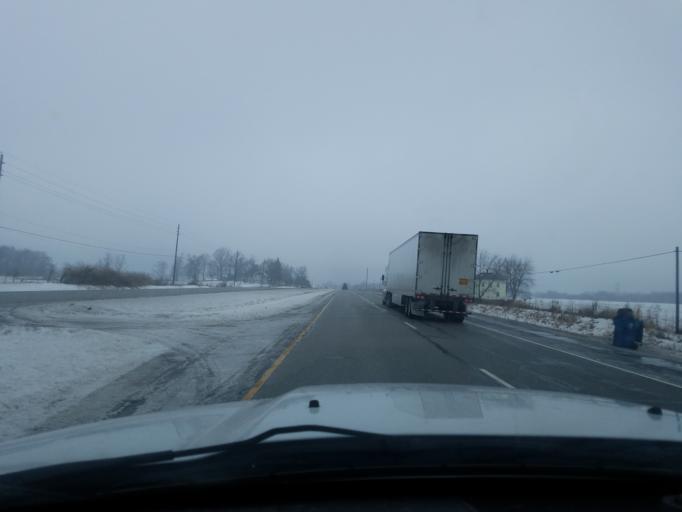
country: US
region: Indiana
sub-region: Miami County
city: Grissom Air Force Base
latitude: 40.7093
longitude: -86.1276
